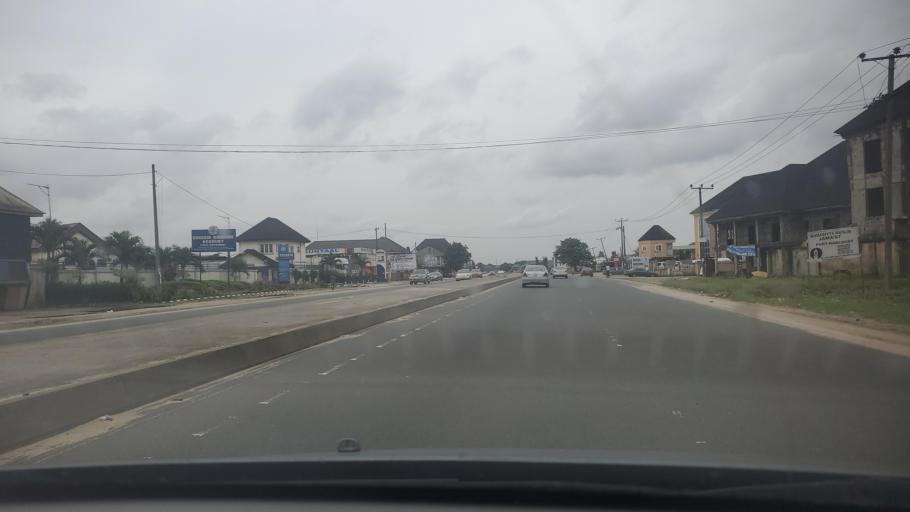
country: NG
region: Rivers
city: Emuoha
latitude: 4.8732
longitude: 6.9601
